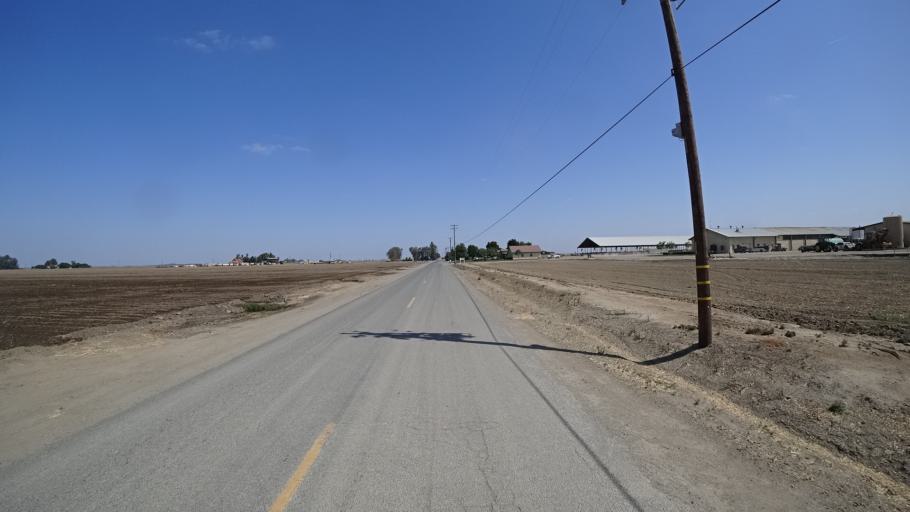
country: US
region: California
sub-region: Kings County
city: Home Garden
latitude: 36.2206
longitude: -119.6278
